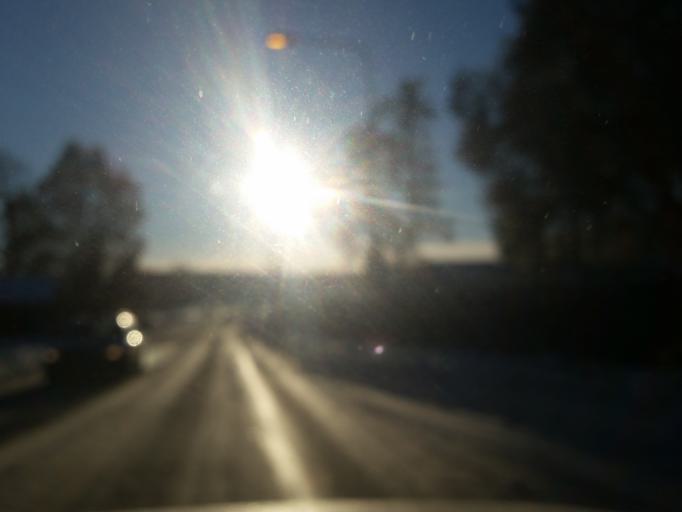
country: SE
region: Vaestmanland
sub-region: Arboga Kommun
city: Arboga
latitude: 59.3928
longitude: 15.8326
